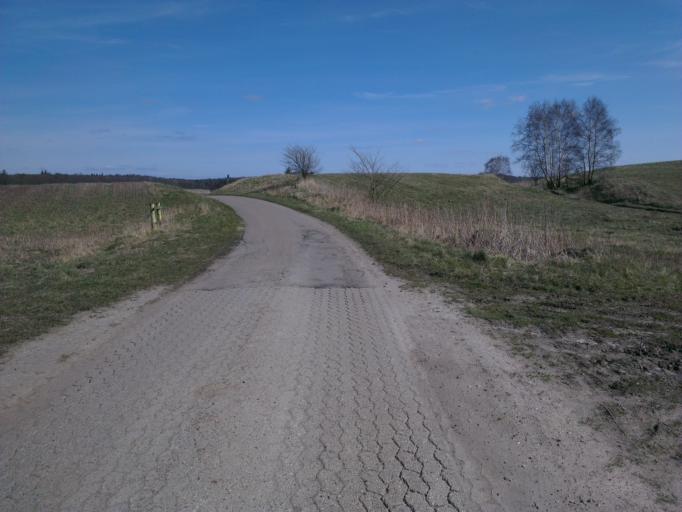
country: DK
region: Capital Region
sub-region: Frederikssund Kommune
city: Jaegerspris
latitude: 55.8945
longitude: 11.9717
